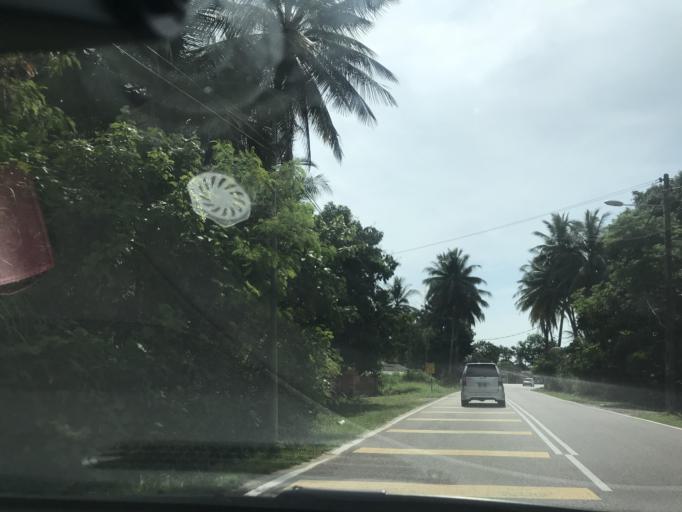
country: MY
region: Kelantan
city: Tumpat
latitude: 6.2020
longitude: 102.1543
